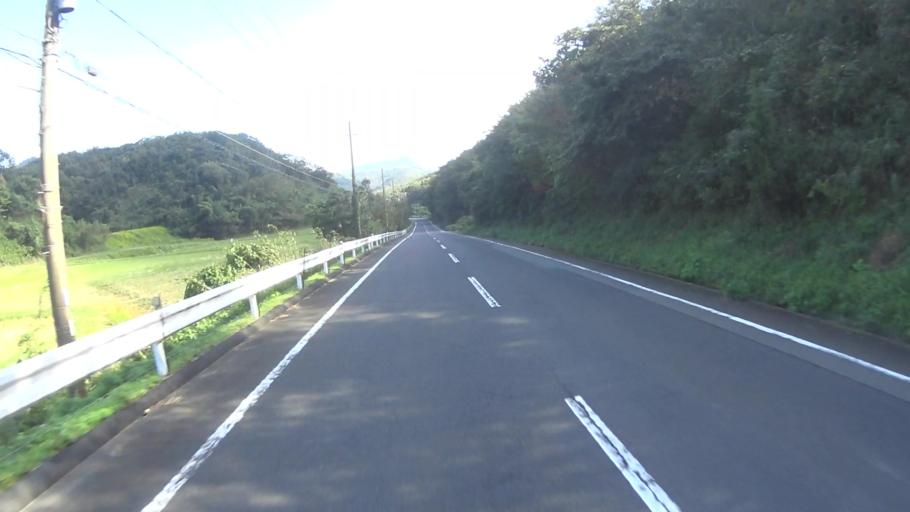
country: JP
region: Kyoto
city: Miyazu
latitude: 35.7031
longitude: 135.0727
